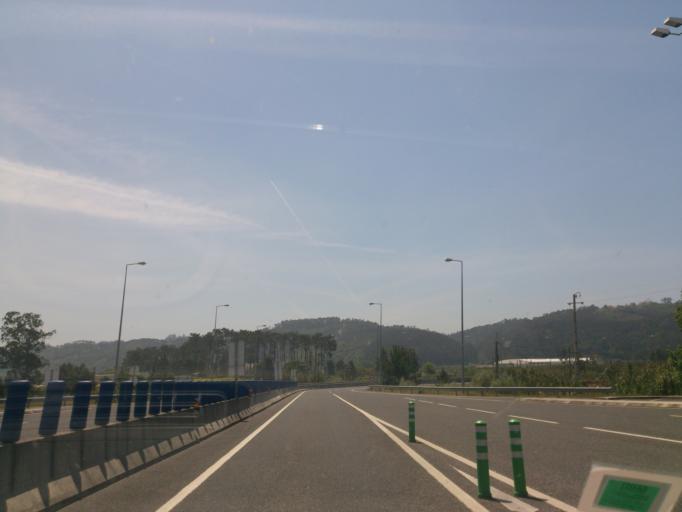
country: PT
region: Leiria
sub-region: Alcobaca
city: Alcobaca
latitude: 39.5842
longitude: -9.0088
